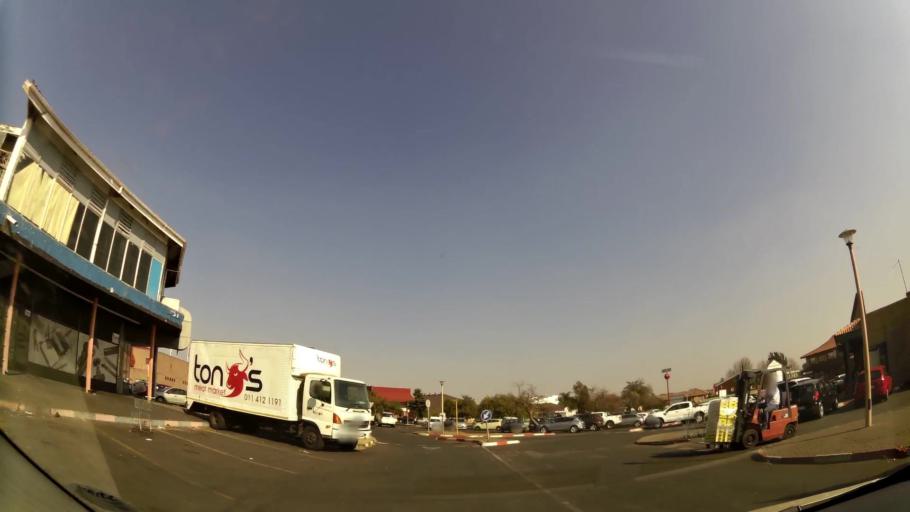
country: ZA
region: Gauteng
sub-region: West Rand District Municipality
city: Randfontein
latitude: -26.1657
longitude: 27.6986
